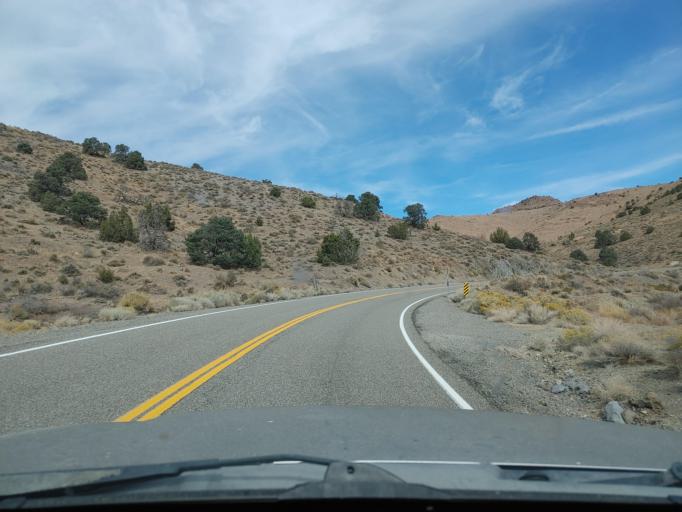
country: US
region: Nevada
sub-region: Storey County
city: Virginia City
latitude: 39.2673
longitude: -119.6314
